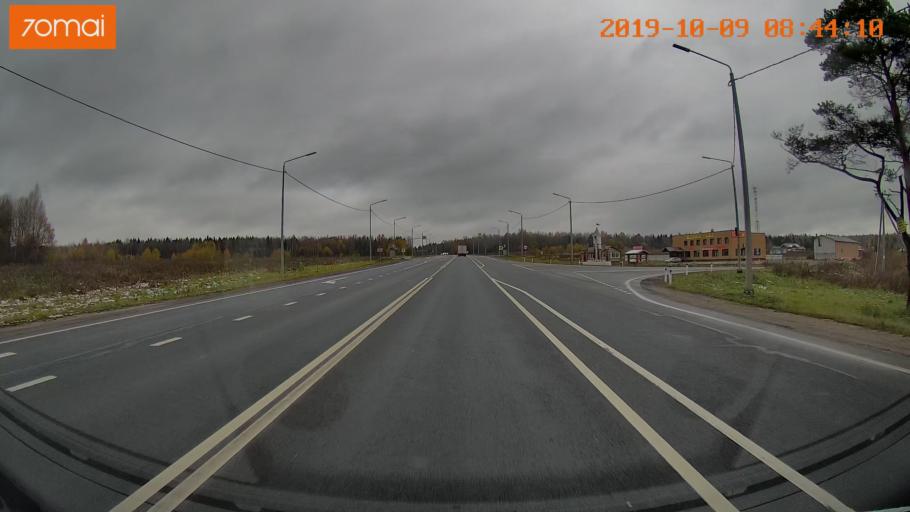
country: RU
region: Vologda
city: Gryazovets
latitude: 59.0327
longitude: 40.1101
